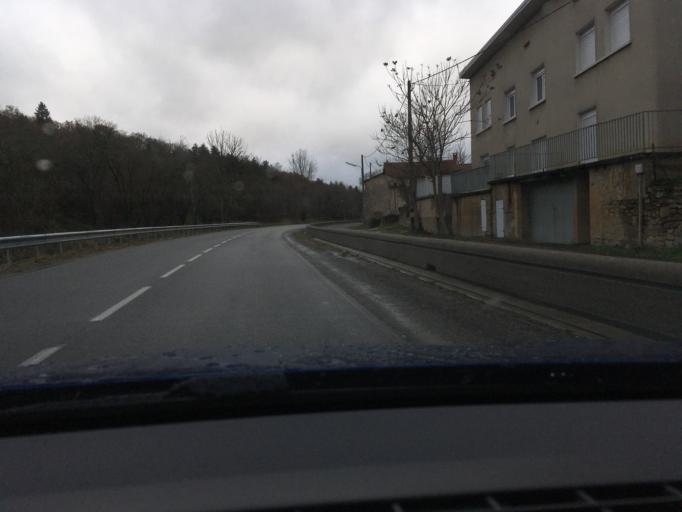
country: FR
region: Midi-Pyrenees
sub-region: Departement de l'Aveyron
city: Villefranche-de-Rouergue
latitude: 44.3666
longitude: 2.0161
